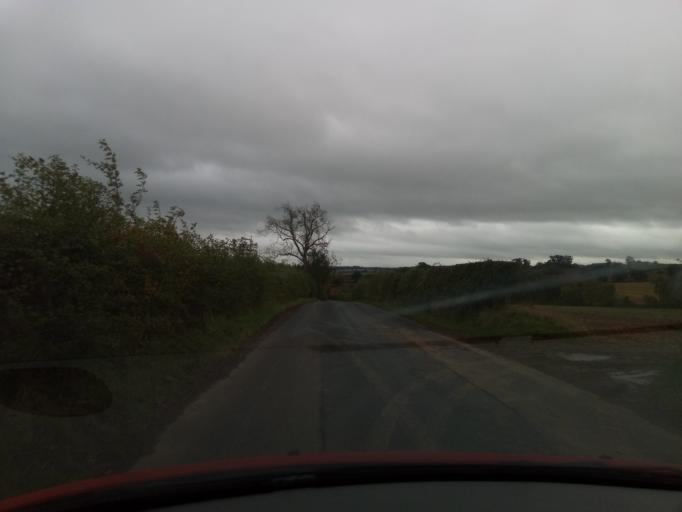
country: GB
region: Scotland
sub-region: The Scottish Borders
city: Saint Boswells
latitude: 55.5198
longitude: -2.6325
